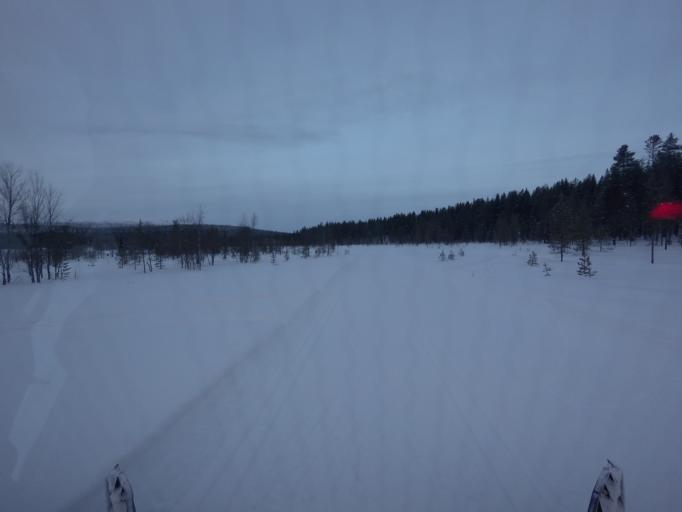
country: FI
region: Lapland
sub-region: Tunturi-Lappi
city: Kolari
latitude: 67.6200
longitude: 24.1376
